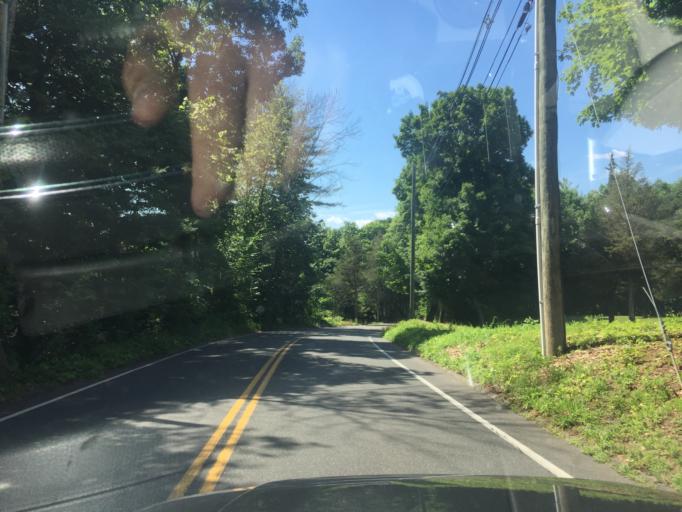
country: US
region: Connecticut
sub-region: Hartford County
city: Farmington
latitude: 41.7609
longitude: -72.8171
